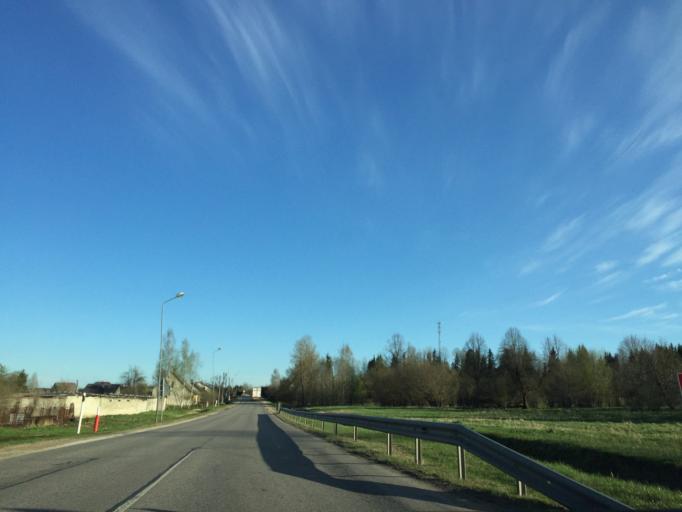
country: LV
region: Valkas Rajons
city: Valka
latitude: 57.7703
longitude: 25.9996
